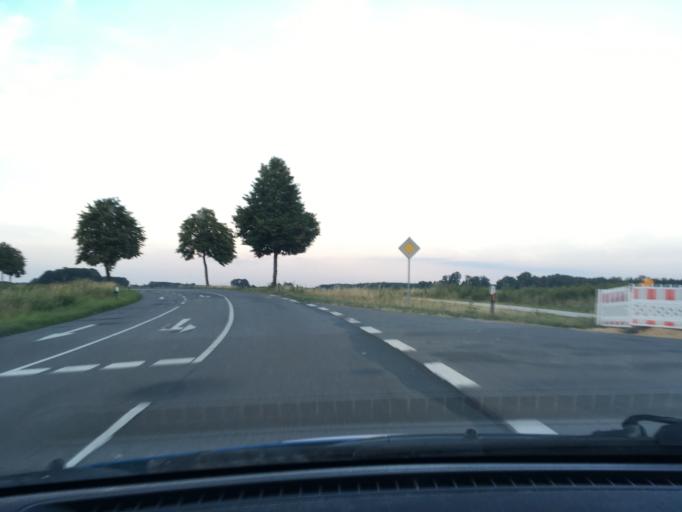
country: DE
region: Lower Saxony
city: Jelmstorf
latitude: 53.1311
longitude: 10.5297
